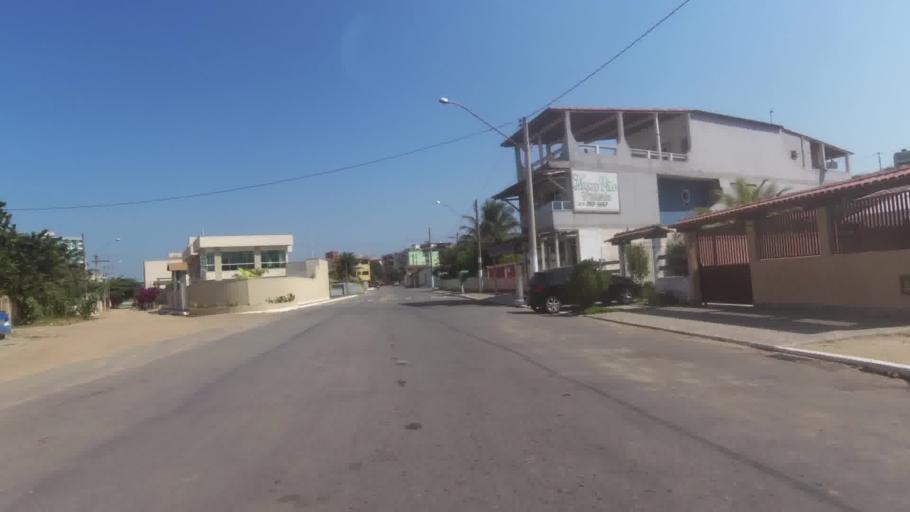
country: BR
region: Espirito Santo
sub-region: Marataizes
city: Marataizes
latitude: -21.0505
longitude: -40.8323
